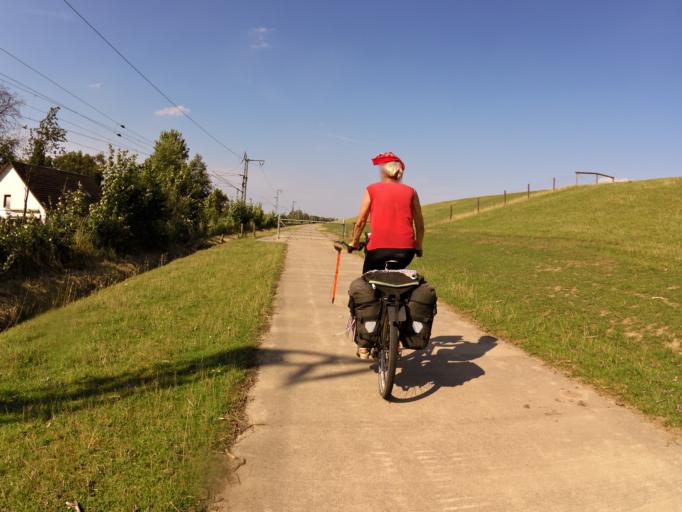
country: DE
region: Lower Saxony
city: Nordenham
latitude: 53.4474
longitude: 8.4758
